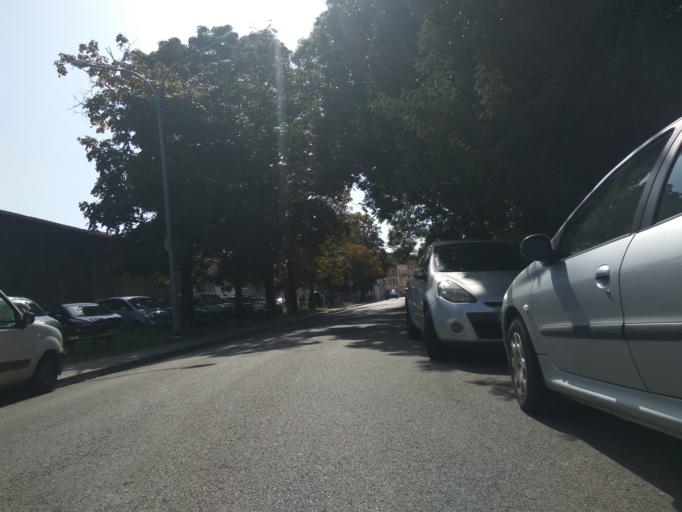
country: FR
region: Aquitaine
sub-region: Departement des Pyrenees-Atlantiques
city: Pau
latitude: 43.3037
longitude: -0.3737
